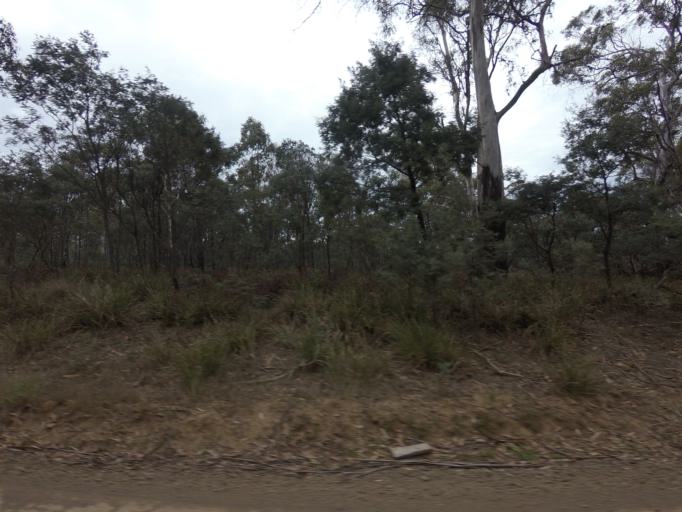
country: AU
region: Tasmania
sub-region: Derwent Valley
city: New Norfolk
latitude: -42.5629
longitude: 146.9406
